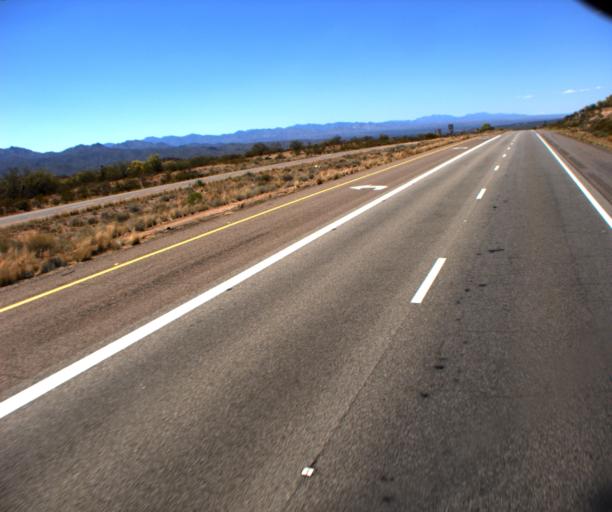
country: US
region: Arizona
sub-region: Yavapai County
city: Bagdad
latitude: 34.6084
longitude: -113.5234
